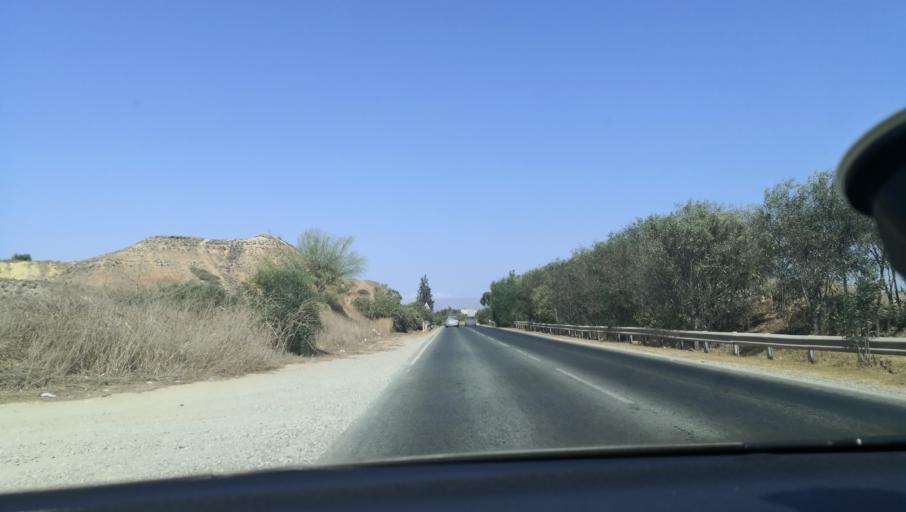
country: CY
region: Lefkosia
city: Kato Deftera
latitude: 35.1063
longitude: 33.2856
